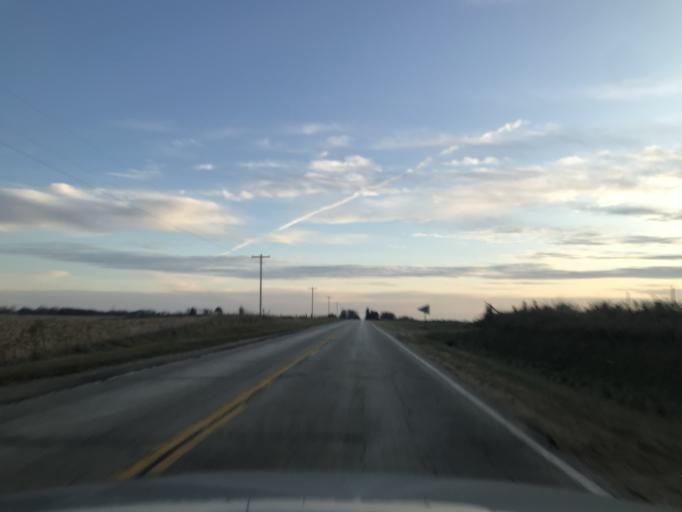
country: US
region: Illinois
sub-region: Henderson County
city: Oquawka
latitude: 40.9498
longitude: -90.8640
